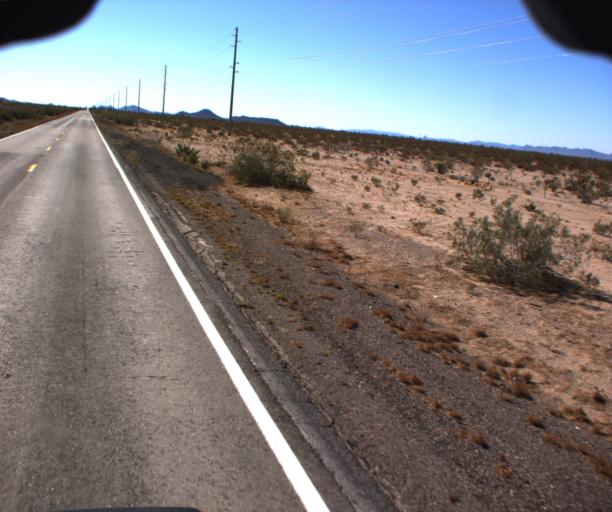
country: US
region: Arizona
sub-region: La Paz County
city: Salome
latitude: 33.8198
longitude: -113.8609
